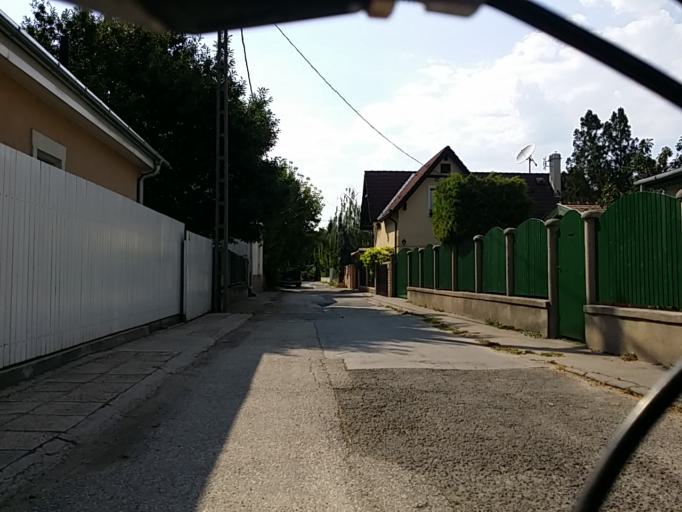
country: HU
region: Budapest
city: Budapest IV. keruelet
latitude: 47.5822
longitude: 19.0597
